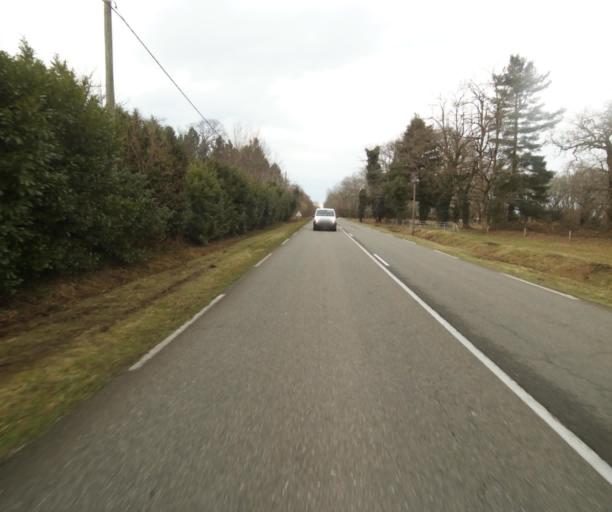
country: FR
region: Aquitaine
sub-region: Departement des Landes
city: Gabarret
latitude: 44.0919
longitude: -0.0214
